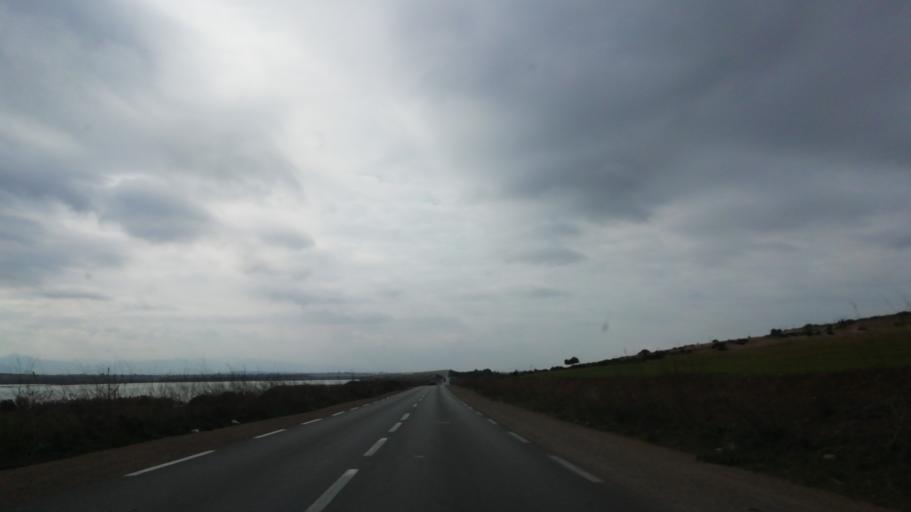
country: DZ
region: Oran
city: Sidi ech Chahmi
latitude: 35.6079
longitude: -0.4306
